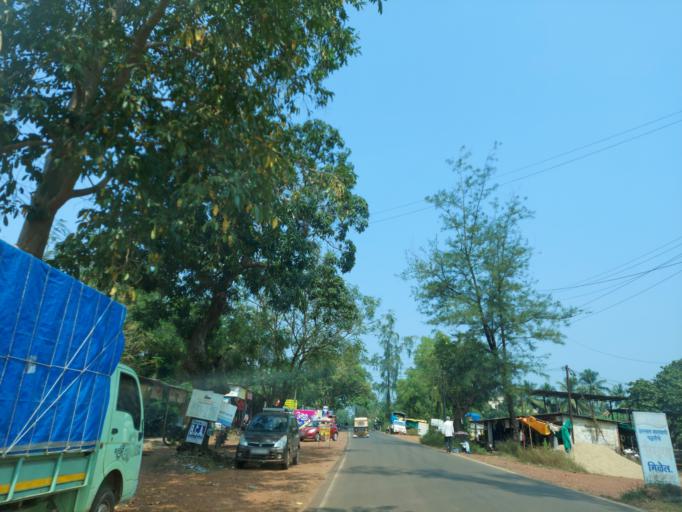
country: IN
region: Maharashtra
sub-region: Sindhudurg
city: Kudal
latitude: 15.9894
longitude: 73.6834
